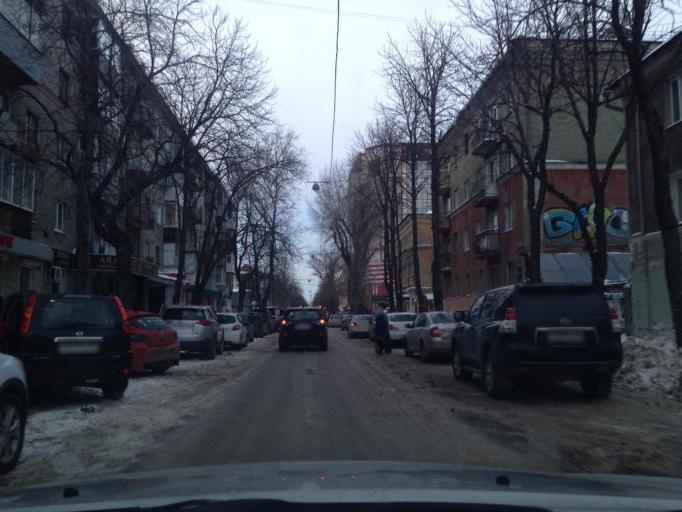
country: RU
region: Voronezj
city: Voronezh
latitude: 51.6684
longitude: 39.2041
